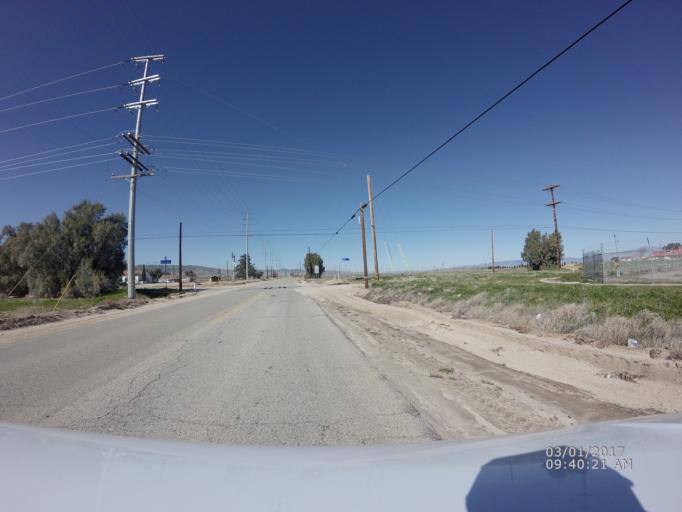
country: US
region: California
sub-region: Los Angeles County
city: Leona Valley
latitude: 34.6893
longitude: -118.2889
